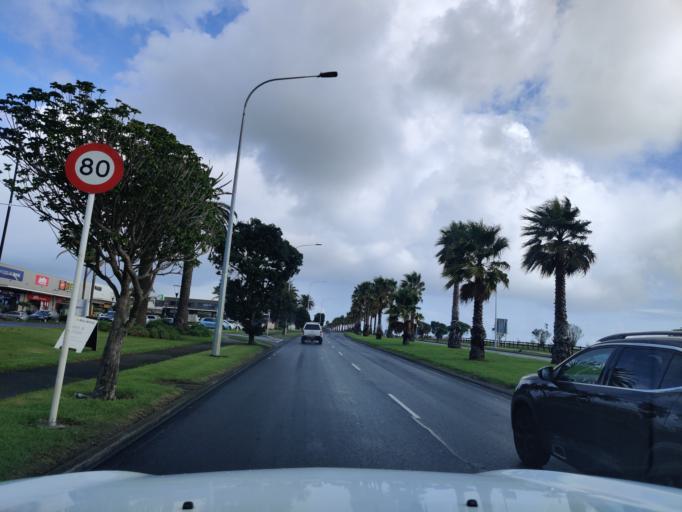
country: NZ
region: Auckland
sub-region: Auckland
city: Manukau City
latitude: -36.9640
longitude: 174.9021
